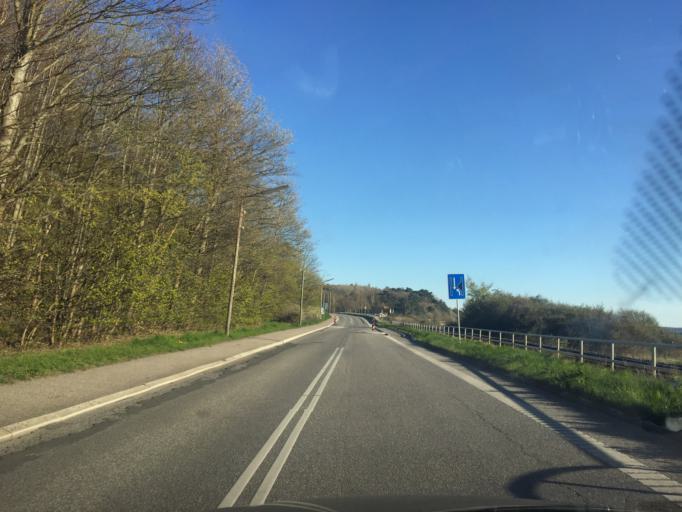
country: DK
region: Capital Region
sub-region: Halsnaes Kommune
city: Frederiksvaerk
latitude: 55.9583
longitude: 12.0199
